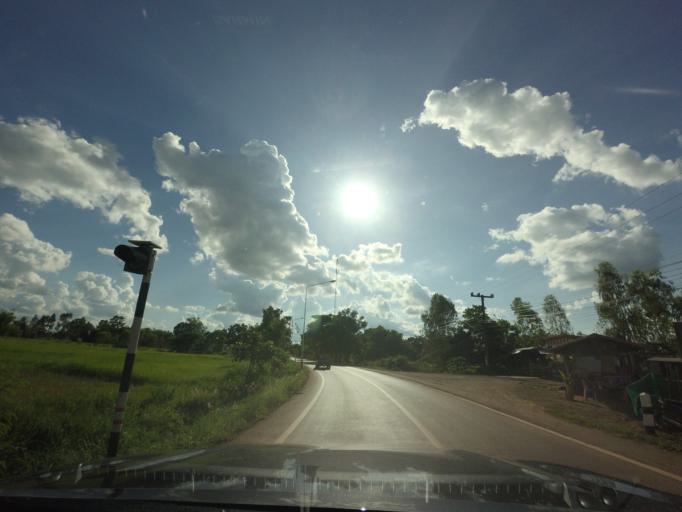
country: TH
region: Changwat Udon Thani
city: Ban Dung
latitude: 17.7460
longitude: 103.3252
